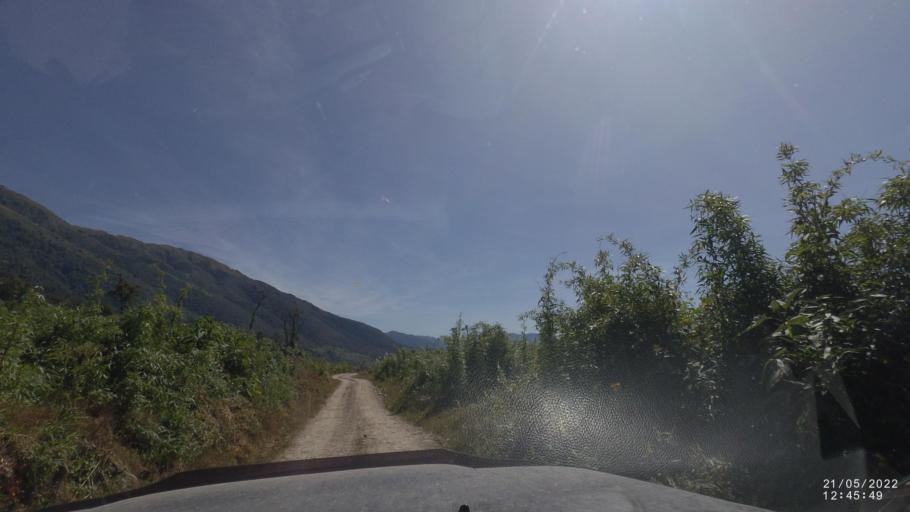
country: BO
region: Cochabamba
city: Colomi
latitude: -17.1865
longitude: -65.9361
